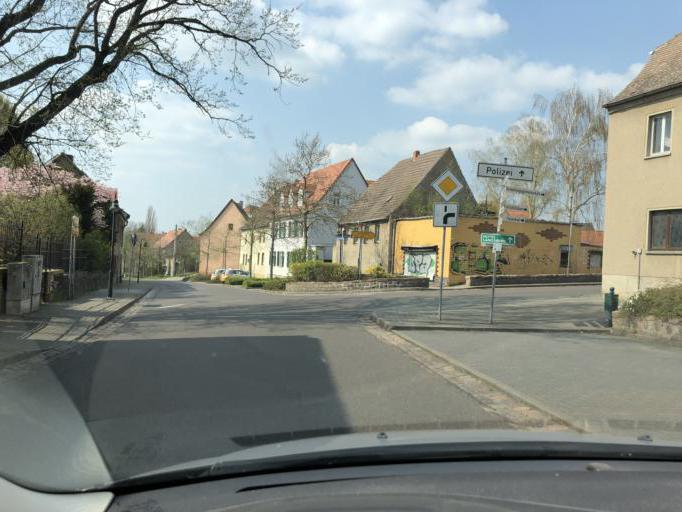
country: DE
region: Saxony-Anhalt
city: Landsberg
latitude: 51.5256
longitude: 12.1585
